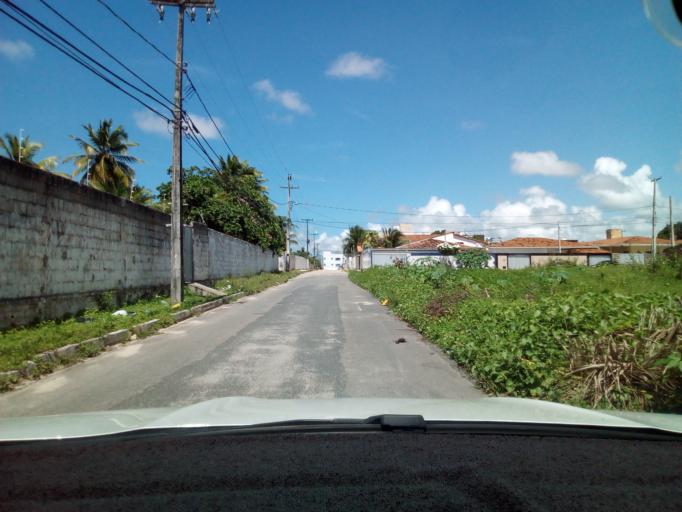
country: BR
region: Paraiba
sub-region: Joao Pessoa
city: Joao Pessoa
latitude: -7.1505
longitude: -34.8296
